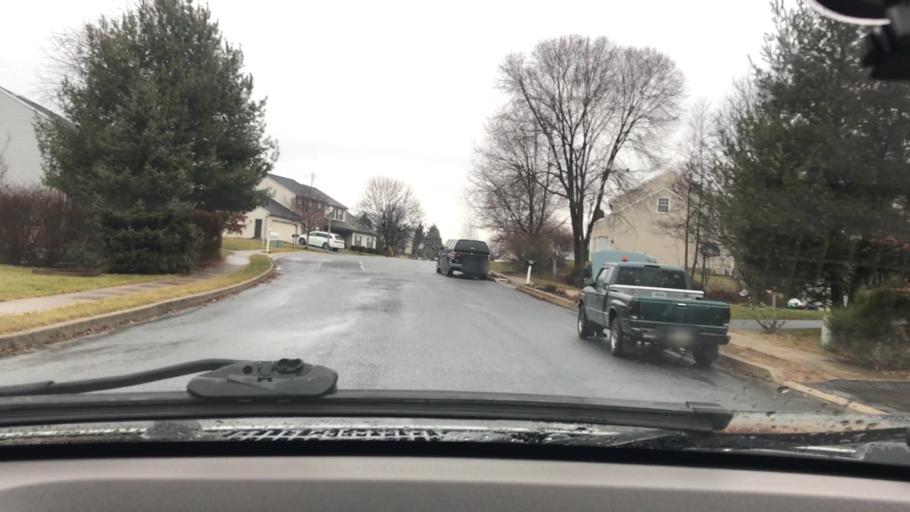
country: US
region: Pennsylvania
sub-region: Lancaster County
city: Elizabethtown
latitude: 40.1660
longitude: -76.5911
